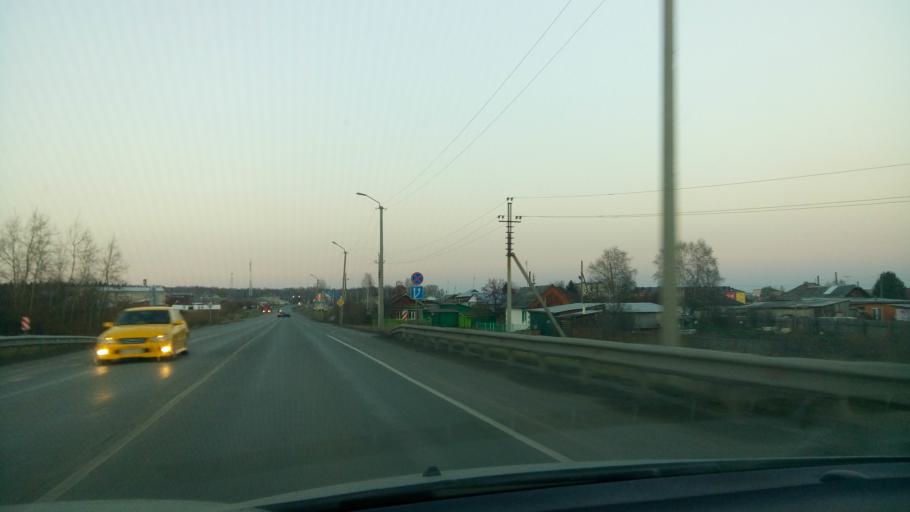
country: RU
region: Sverdlovsk
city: Pyshma
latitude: 56.9465
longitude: 63.2225
